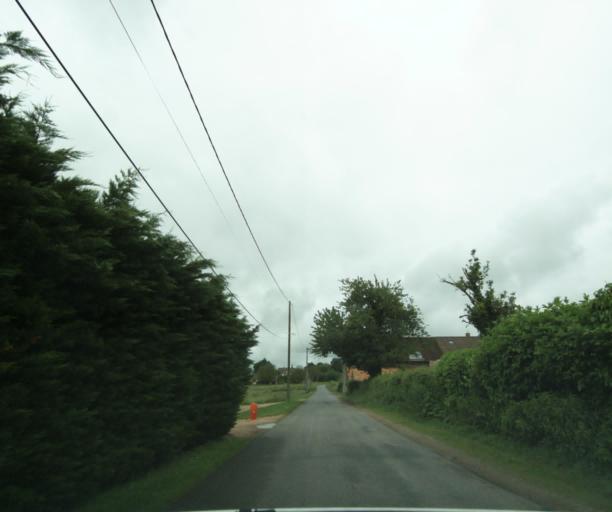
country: FR
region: Bourgogne
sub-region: Departement de Saone-et-Loire
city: Charolles
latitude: 46.4498
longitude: 4.3423
